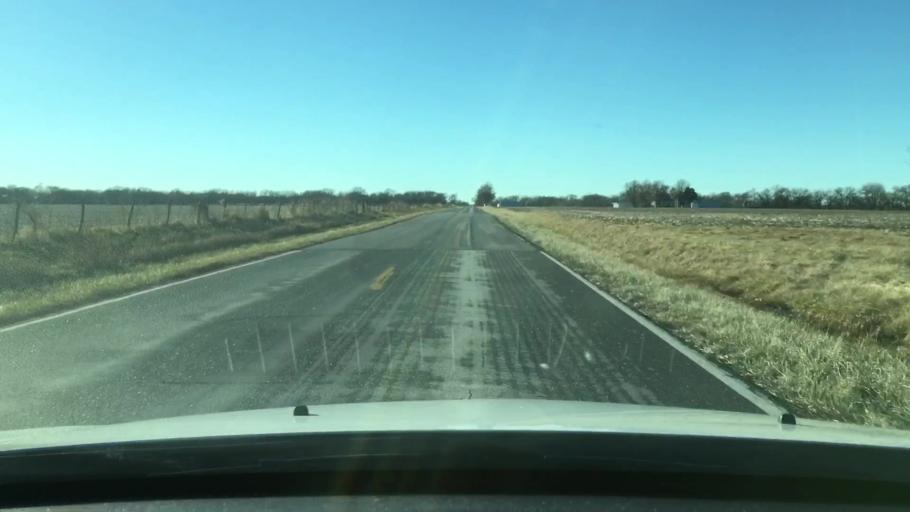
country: US
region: Missouri
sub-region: Audrain County
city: Mexico
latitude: 39.2815
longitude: -91.7049
